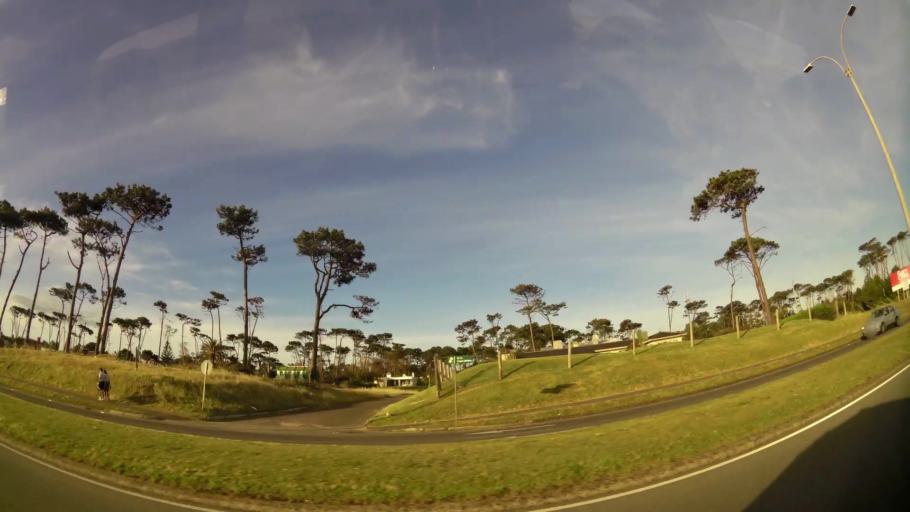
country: UY
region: Maldonado
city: Maldonado
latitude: -34.9127
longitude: -54.9879
